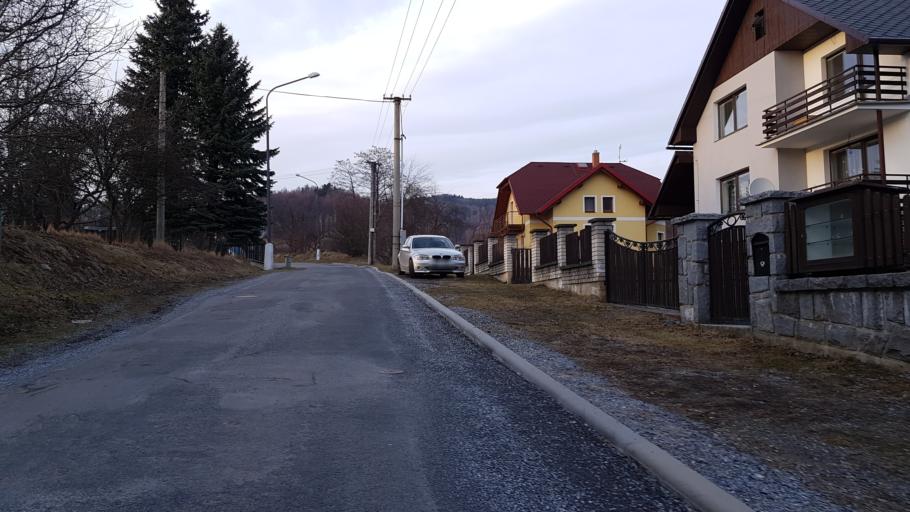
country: CZ
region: Olomoucky
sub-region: Okres Jesenik
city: Jesenik
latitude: 50.2291
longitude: 17.1869
